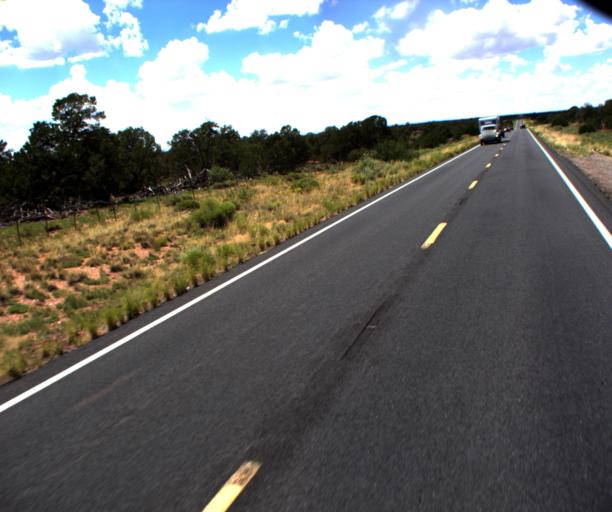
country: US
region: Arizona
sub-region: Coconino County
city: Parks
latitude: 35.6001
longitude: -112.0240
